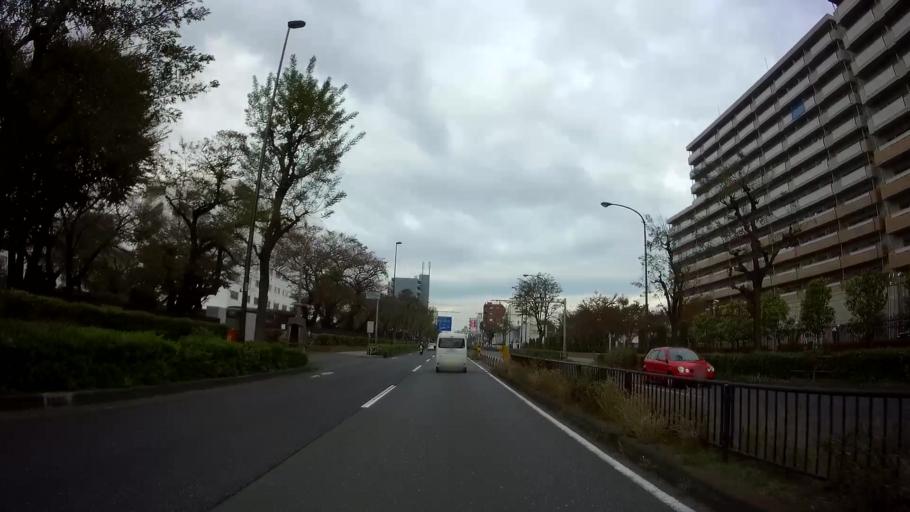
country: JP
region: Saitama
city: Wako
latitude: 35.7653
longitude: 139.6589
